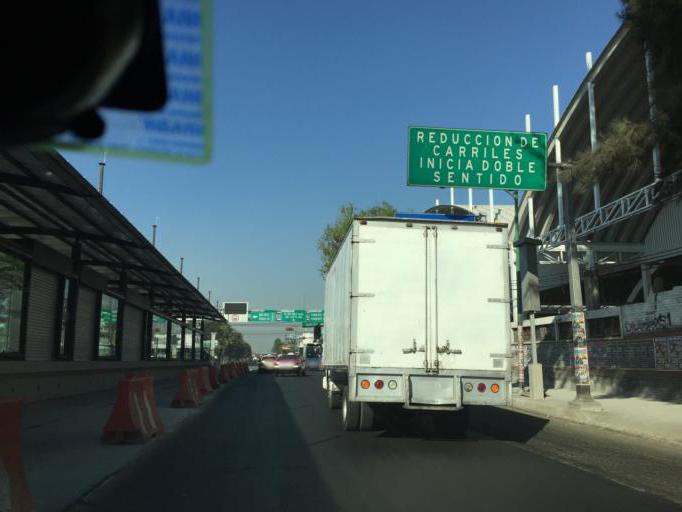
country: MX
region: Mexico
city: Colonia Lindavista
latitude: 19.4949
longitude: -99.1529
